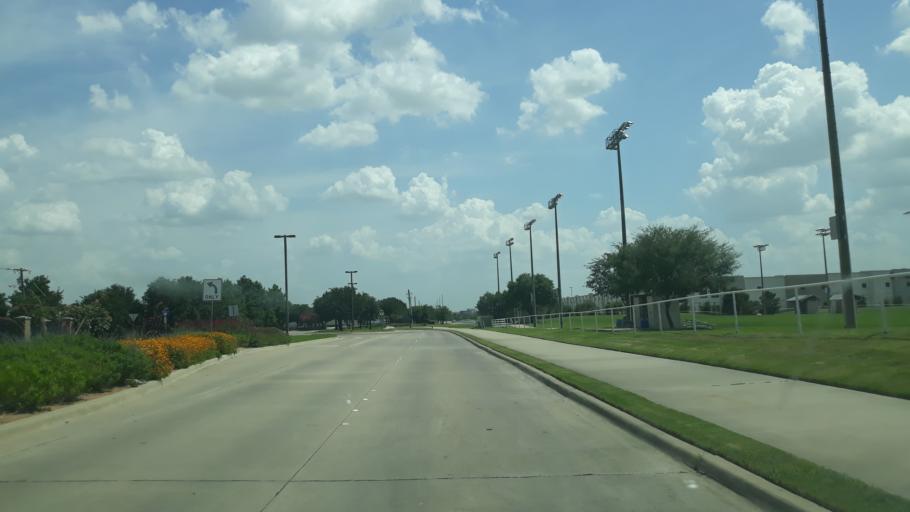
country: US
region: Texas
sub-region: Dallas County
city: Coppell
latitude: 32.9629
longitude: -97.0152
